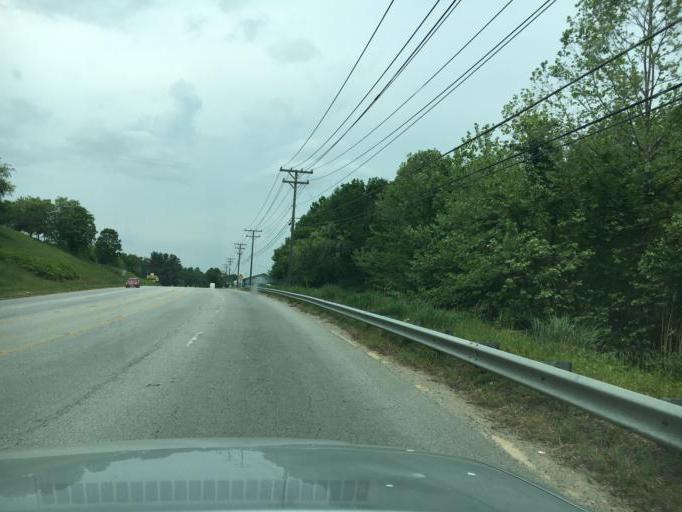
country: US
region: North Carolina
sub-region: Henderson County
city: Balfour
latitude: 35.3585
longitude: -82.4775
